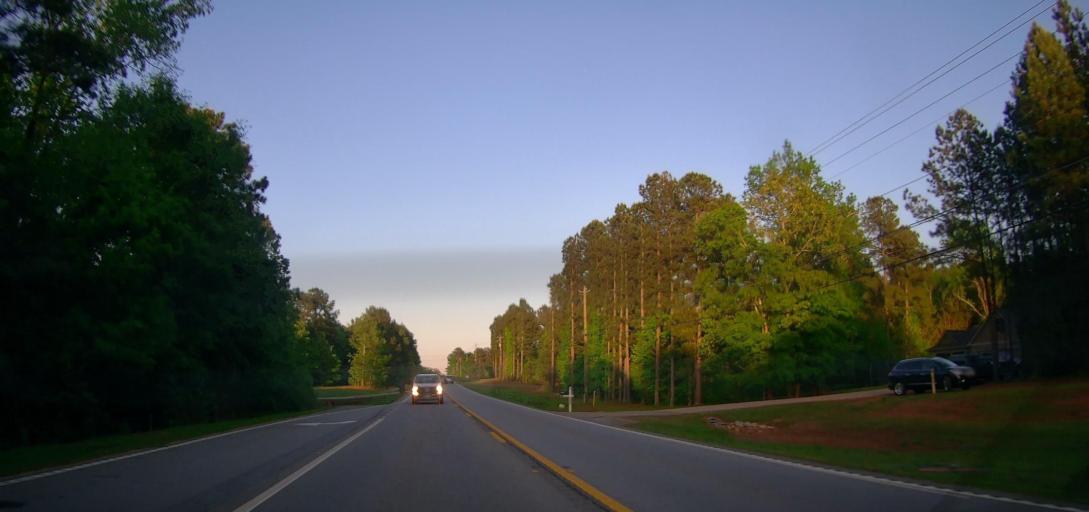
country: US
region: Georgia
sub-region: Newton County
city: Oakwood
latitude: 33.4395
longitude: -84.0199
